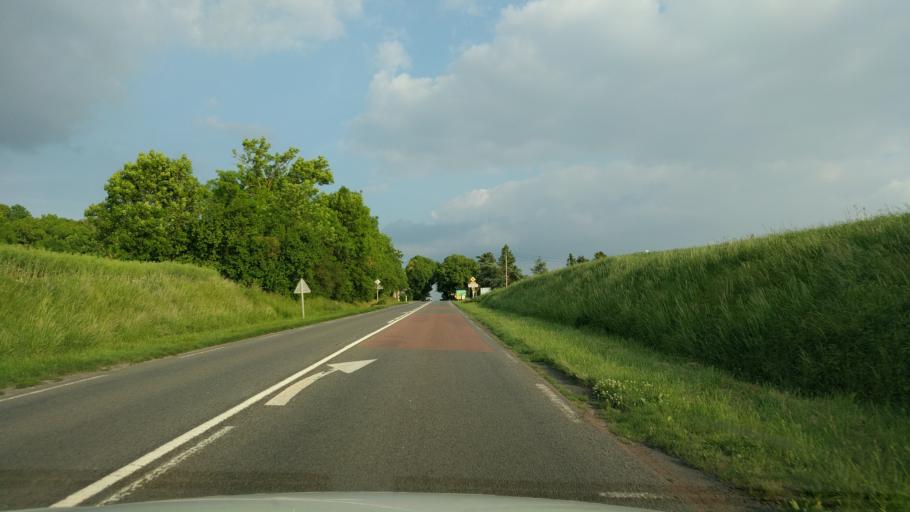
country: FR
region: Picardie
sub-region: Departement de la Somme
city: Peronne
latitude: 49.9493
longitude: 2.9302
